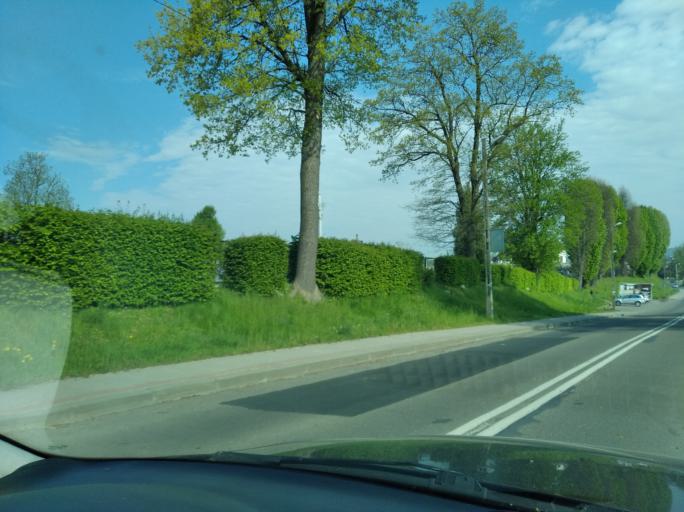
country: PL
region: Subcarpathian Voivodeship
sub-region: Powiat rzeszowski
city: Dynow
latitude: 49.8213
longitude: 22.2346
